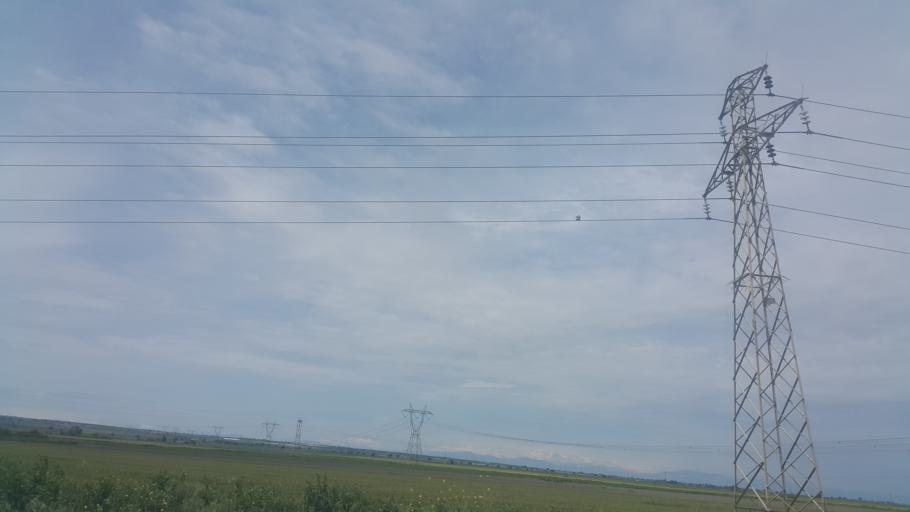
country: TR
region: Adana
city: Yakapinar
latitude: 37.0110
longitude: 35.7051
